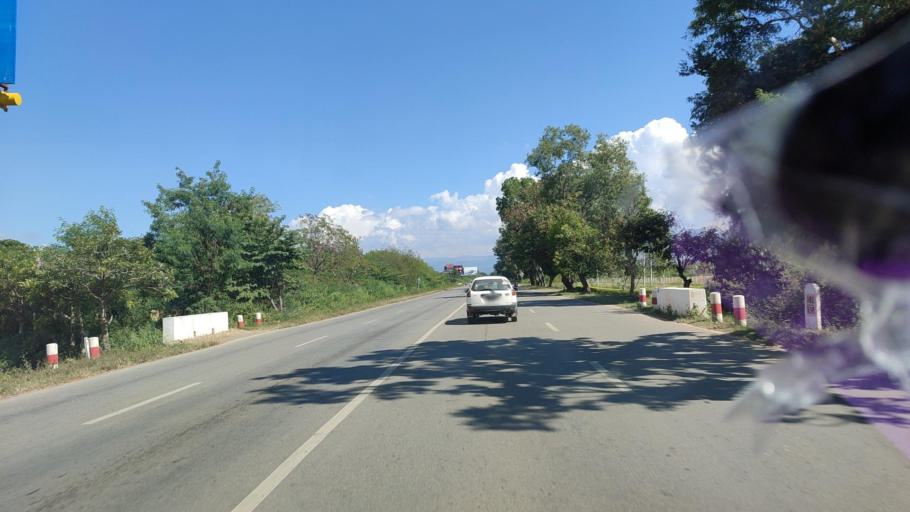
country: MM
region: Shan
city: Taunggyi
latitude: 20.7494
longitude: 96.9115
